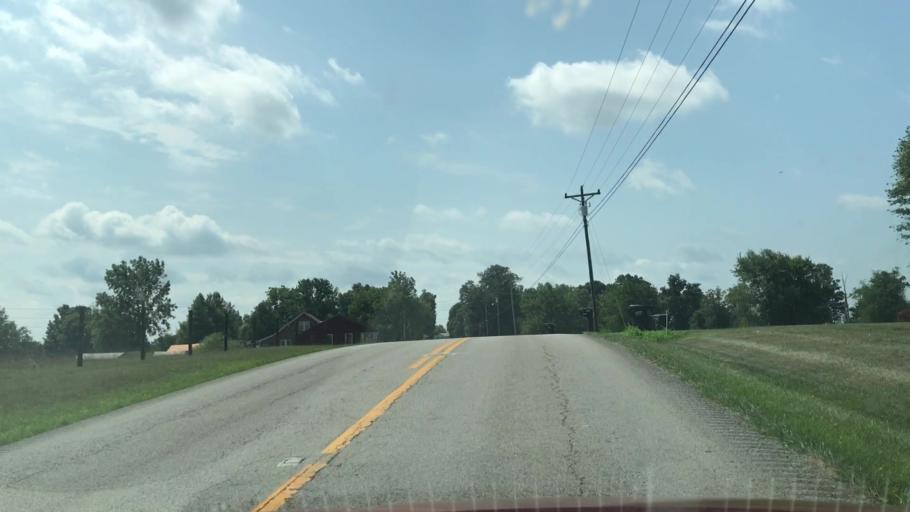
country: US
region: Kentucky
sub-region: Barren County
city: Glasgow
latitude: 36.8934
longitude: -85.8561
